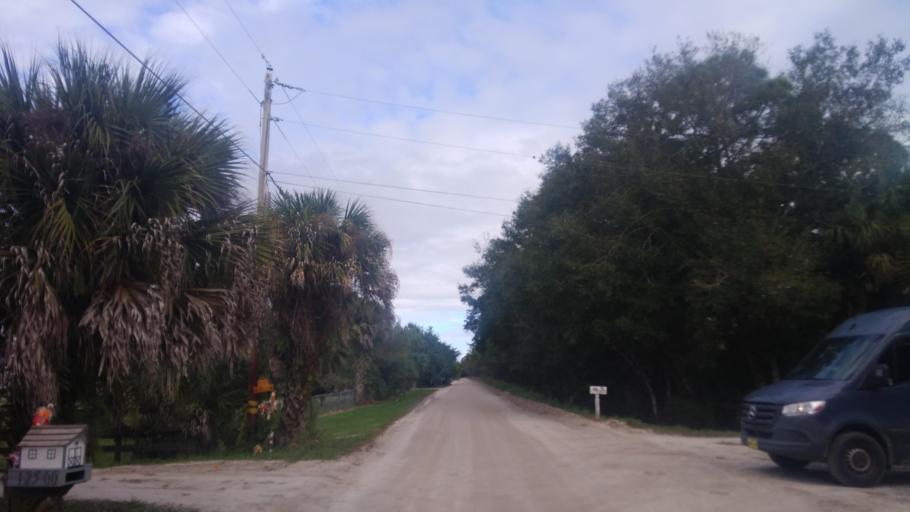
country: US
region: Florida
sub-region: Indian River County
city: Fellsmere
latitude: 27.7609
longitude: -80.5829
